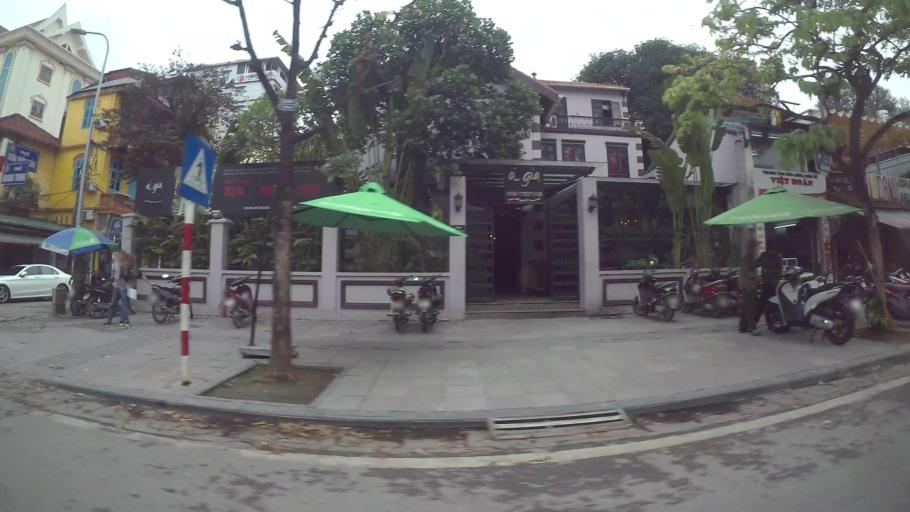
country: VN
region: Ha Noi
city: Hai BaTrung
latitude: 21.0203
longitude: 105.8480
